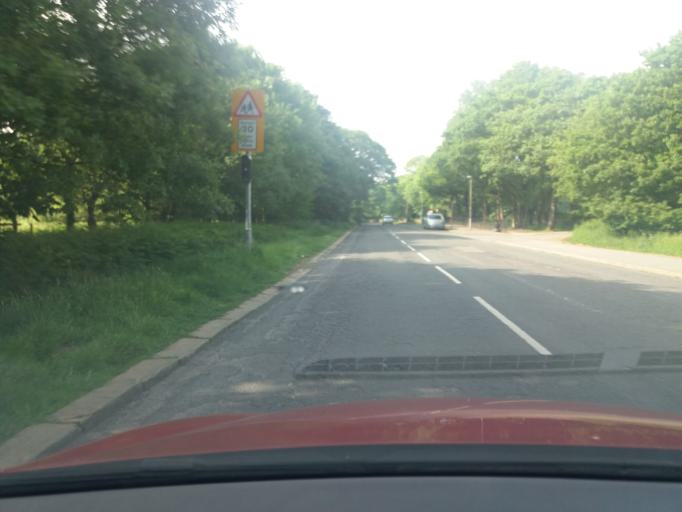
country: GB
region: England
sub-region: Borough of Bolton
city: Horwich
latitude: 53.6080
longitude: -2.5512
